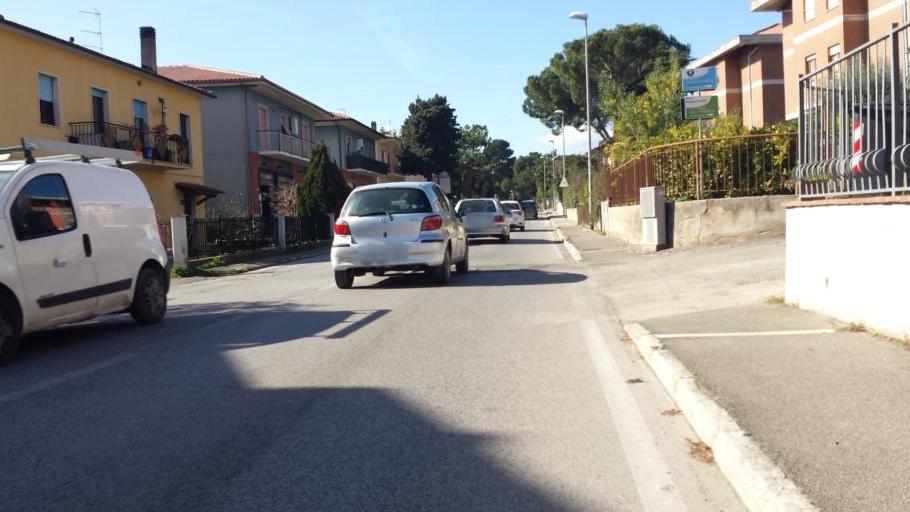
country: IT
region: Umbria
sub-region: Provincia di Terni
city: San Gemini
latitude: 42.5911
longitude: 12.5925
